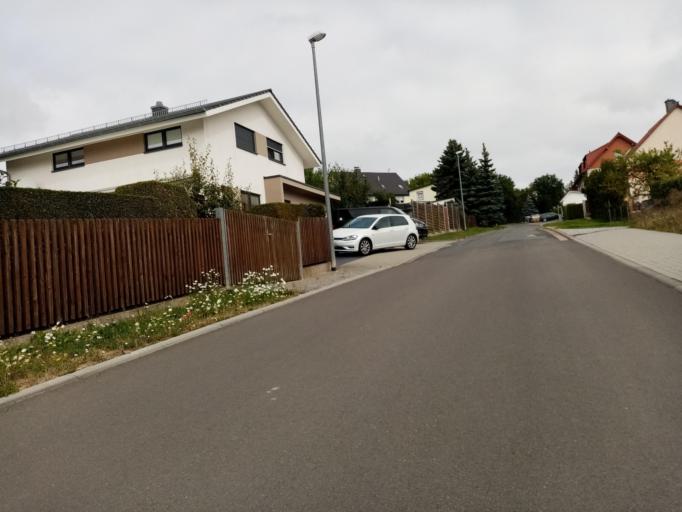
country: DE
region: Thuringia
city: Dingelstadt
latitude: 51.3228
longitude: 10.3183
